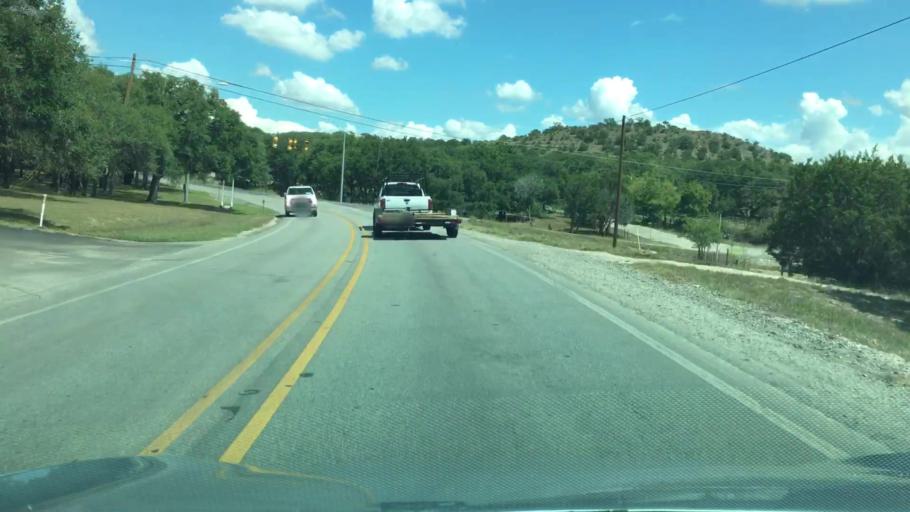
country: US
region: Texas
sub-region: Hays County
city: Wimberley
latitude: 29.9987
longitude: -98.0854
